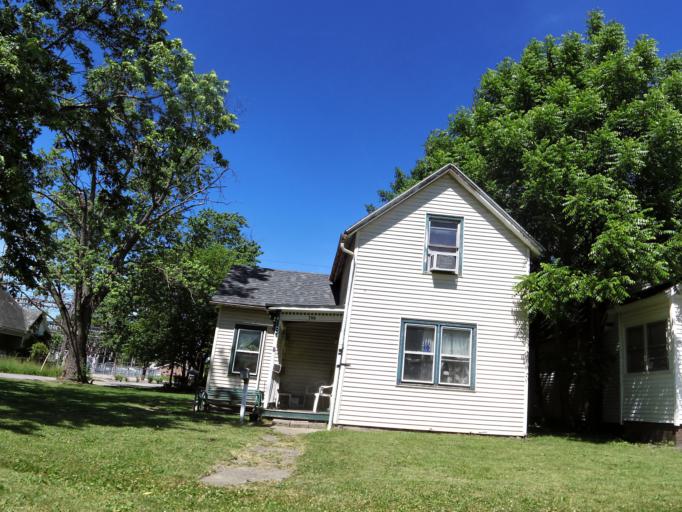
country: US
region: Illinois
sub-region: Vermilion County
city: Danville
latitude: 40.1362
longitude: -87.6315
